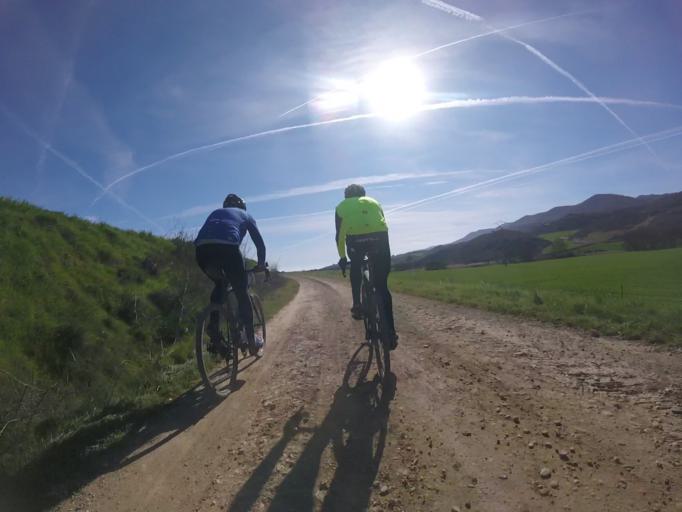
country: ES
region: Navarre
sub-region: Provincia de Navarra
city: Cirauqui
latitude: 42.6664
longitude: -1.9026
